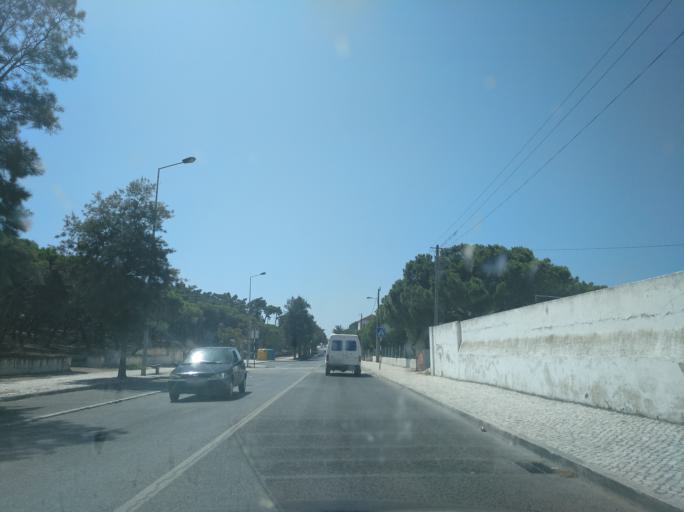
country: PT
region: Setubal
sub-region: Almada
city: Trafaria
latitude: 38.6696
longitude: -9.2382
